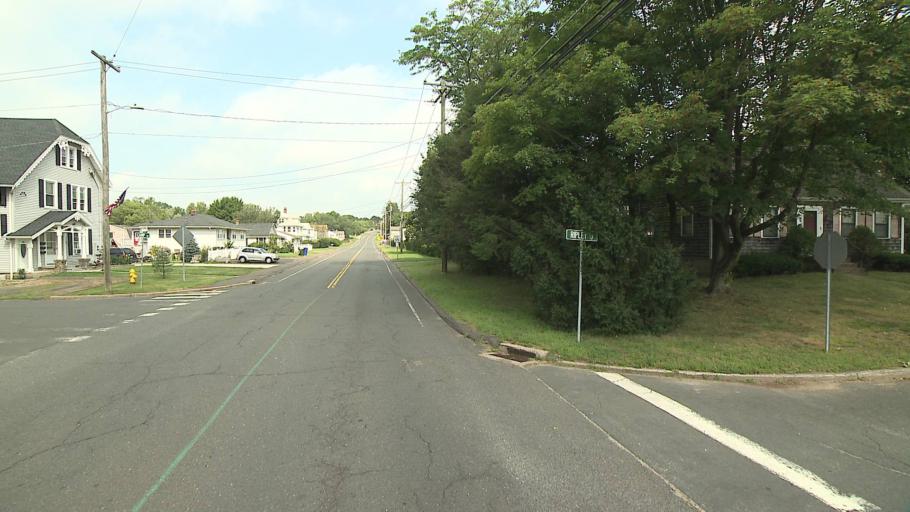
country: US
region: Connecticut
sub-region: Litchfield County
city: Oakville
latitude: 41.5957
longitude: -73.0840
